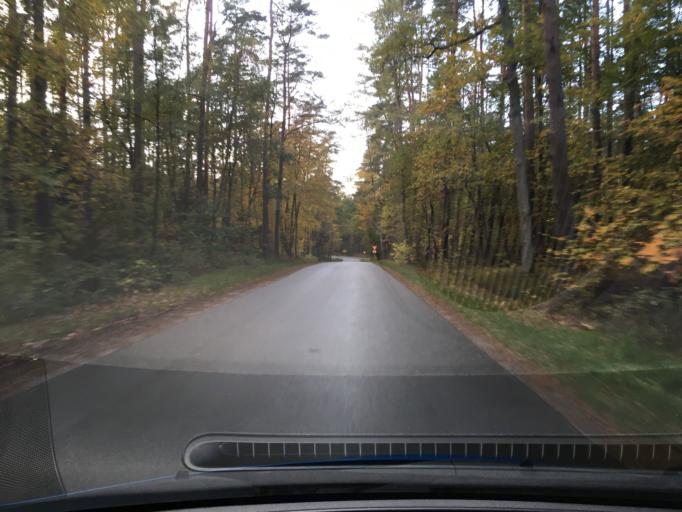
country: DE
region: Lower Saxony
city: Barendorf
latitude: 53.2521
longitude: 10.5311
